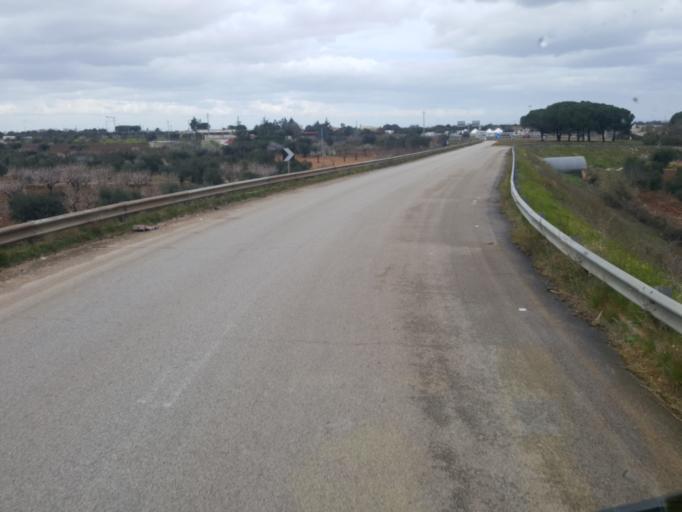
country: IT
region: Apulia
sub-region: Provincia di Bari
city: Conversano
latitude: 40.9806
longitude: 17.0857
